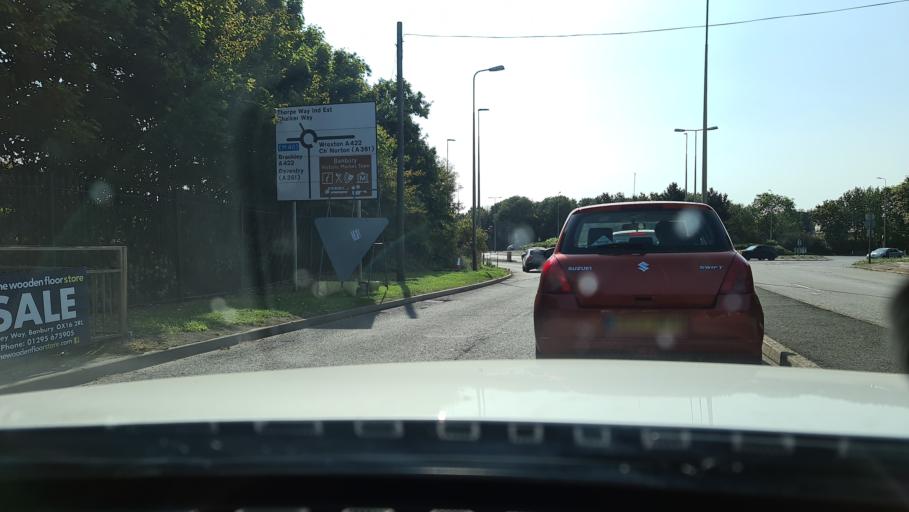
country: GB
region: England
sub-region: Oxfordshire
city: Banbury
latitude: 52.0731
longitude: -1.3191
